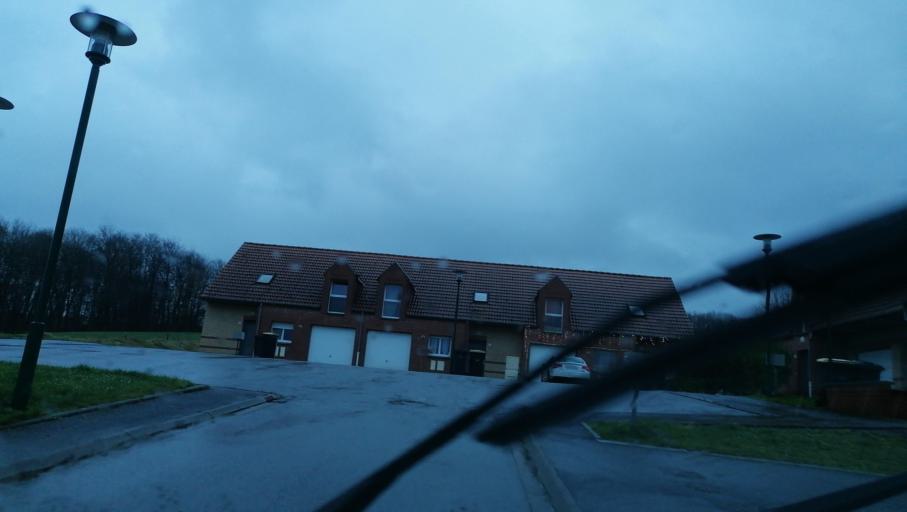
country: FR
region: Nord-Pas-de-Calais
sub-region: Departement du Nord
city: Boussois
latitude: 50.2822
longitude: 4.0573
